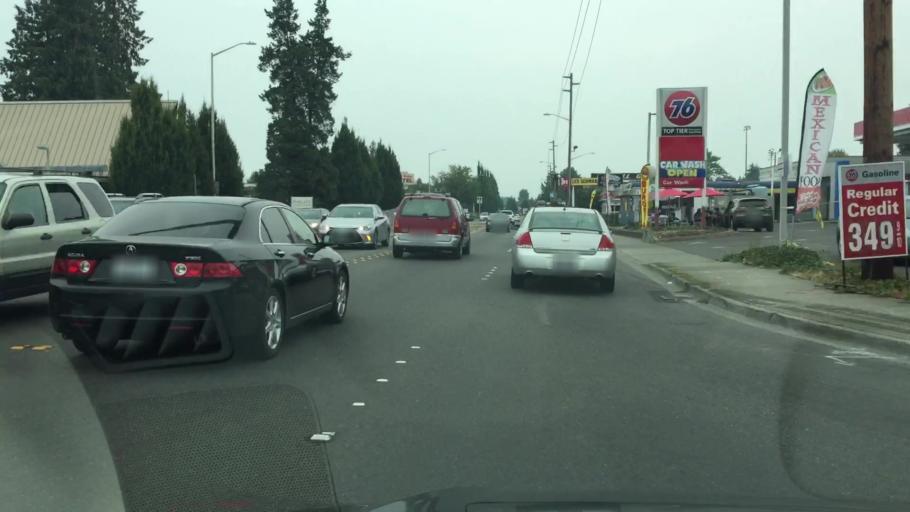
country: US
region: Washington
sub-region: King County
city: Kent
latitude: 47.3868
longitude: -122.2310
